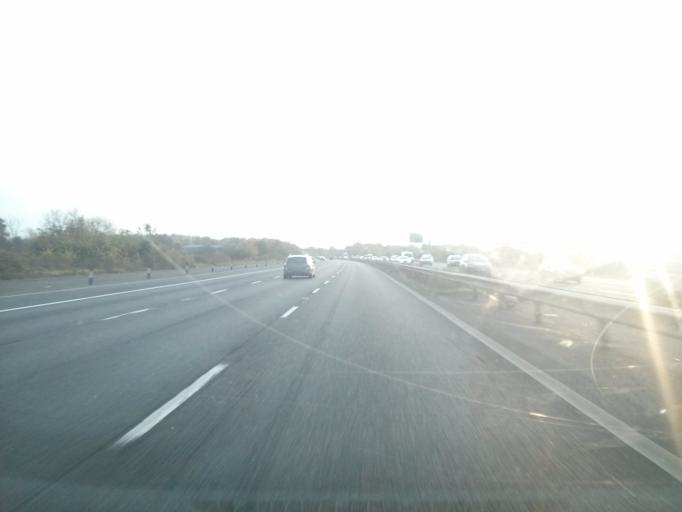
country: GB
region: England
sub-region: Gloucestershire
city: Stonehouse
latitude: 51.7826
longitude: -2.3049
